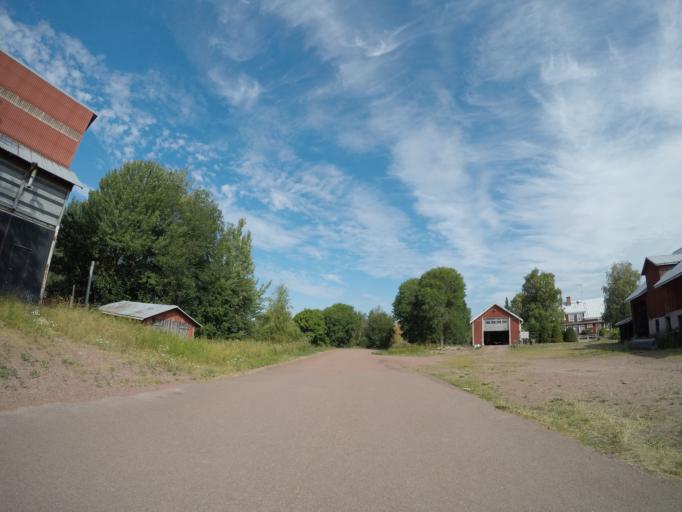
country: AX
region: Alands landsbygd
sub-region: Finstroem
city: Finstroem
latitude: 60.2055
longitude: 19.8743
